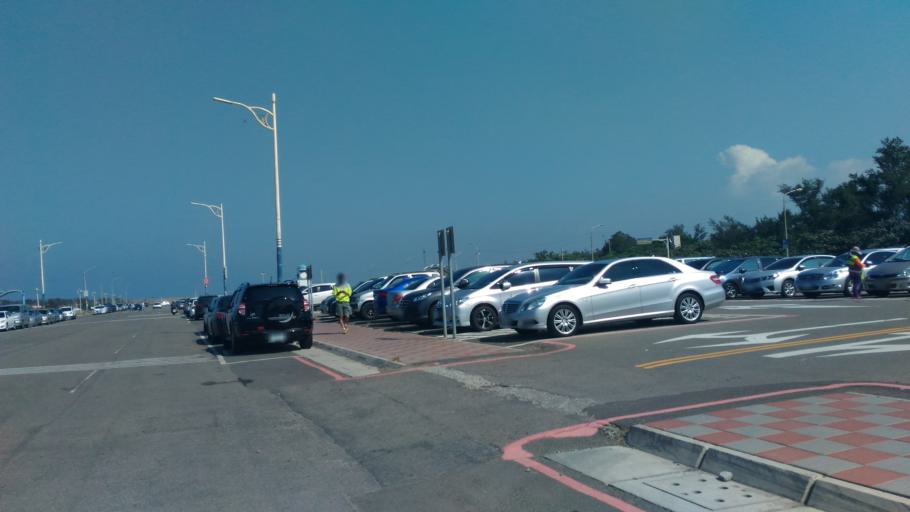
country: TW
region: Taiwan
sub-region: Hsinchu
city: Hsinchu
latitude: 24.8487
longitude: 120.9267
